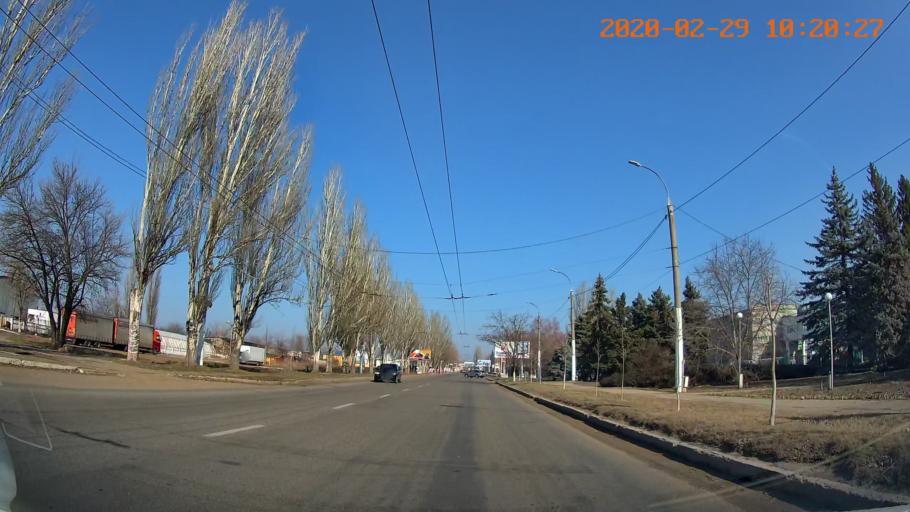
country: MD
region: Telenesti
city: Tiraspolul Nou
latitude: 46.8604
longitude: 29.6106
